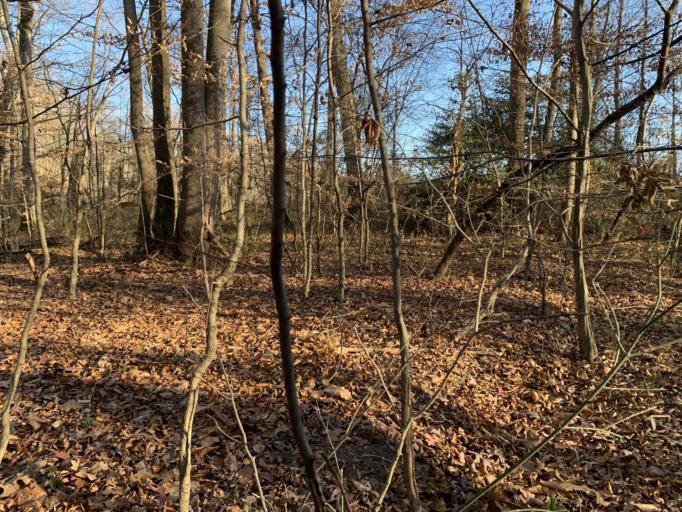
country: US
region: Delaware
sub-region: New Castle County
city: Townsend
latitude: 39.3355
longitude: -75.7356
